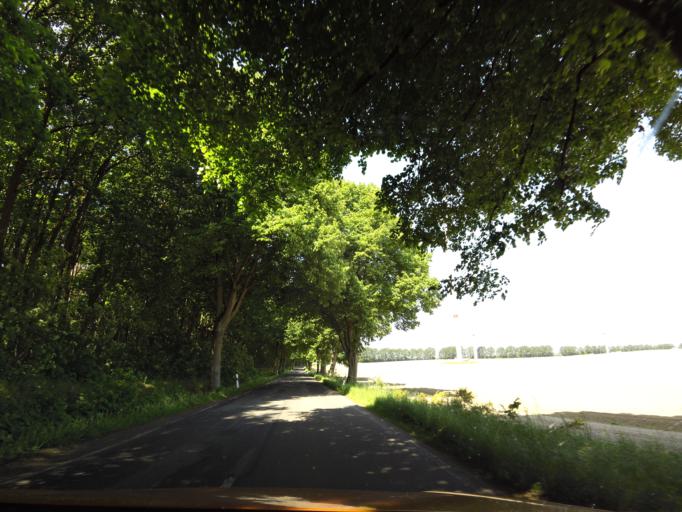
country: DE
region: Mecklenburg-Vorpommern
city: Neuburg
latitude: 53.4112
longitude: 11.8942
